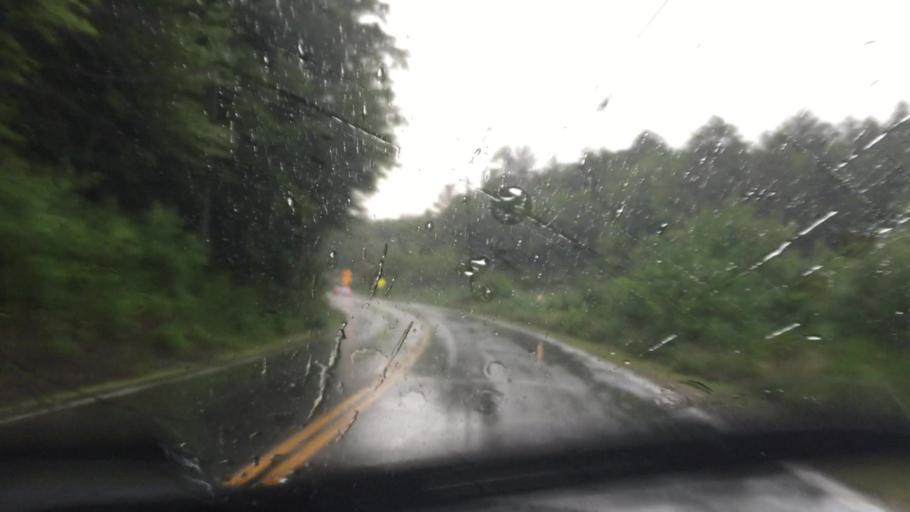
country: US
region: New Hampshire
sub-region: Belknap County
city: Meredith
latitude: 43.6913
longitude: -71.5126
